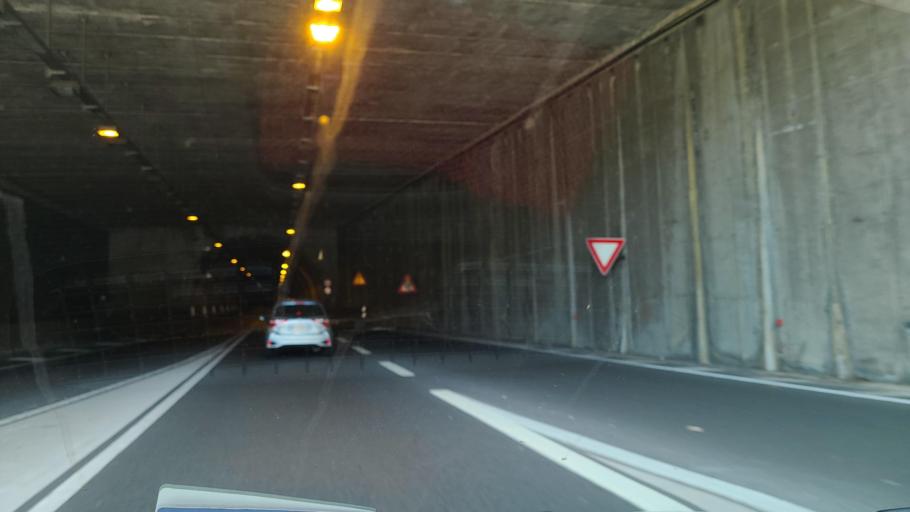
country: IT
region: Liguria
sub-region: Provincia di Imperia
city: San Remo
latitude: 43.8304
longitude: 7.7951
